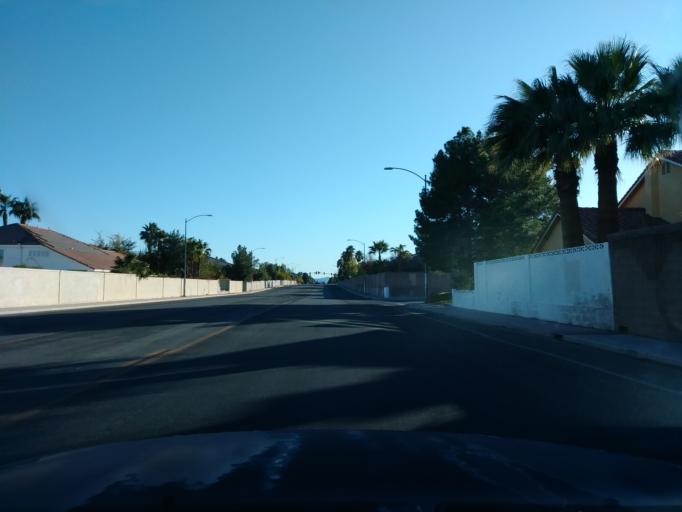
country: US
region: Nevada
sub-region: Clark County
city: Spring Valley
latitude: 36.1544
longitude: -115.2709
